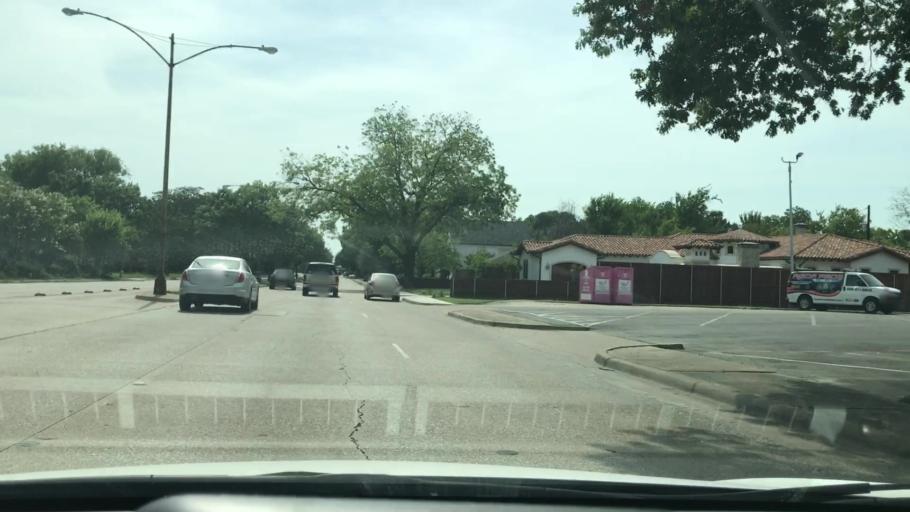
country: US
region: Texas
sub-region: Dallas County
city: University Park
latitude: 32.8801
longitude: -96.7974
